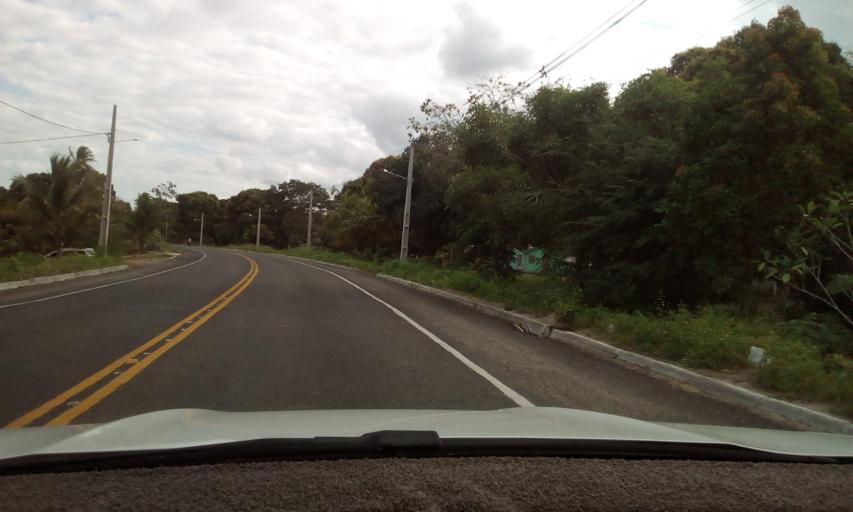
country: BR
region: Paraiba
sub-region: Mamanguape
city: Mamanguape
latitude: -6.8222
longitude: -35.1072
